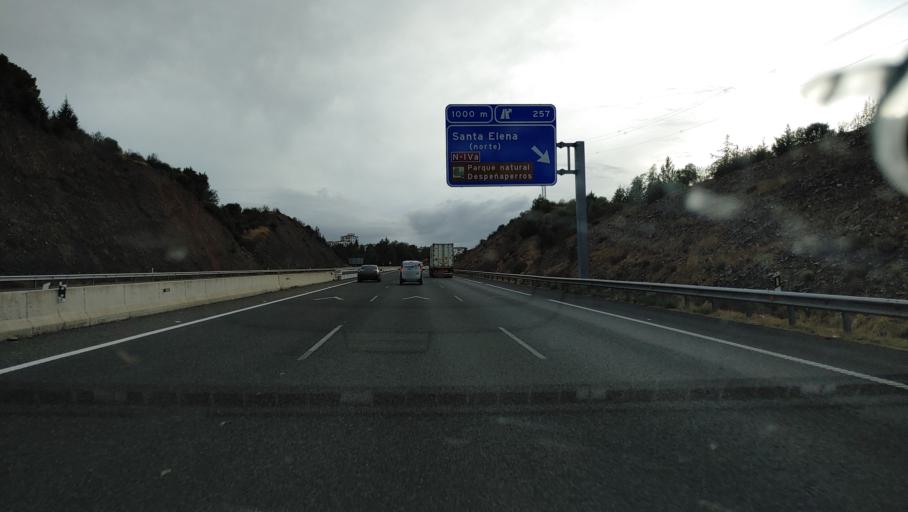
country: ES
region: Andalusia
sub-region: Provincia de Jaen
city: Santa Elena
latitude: 38.3491
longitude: -3.5321
